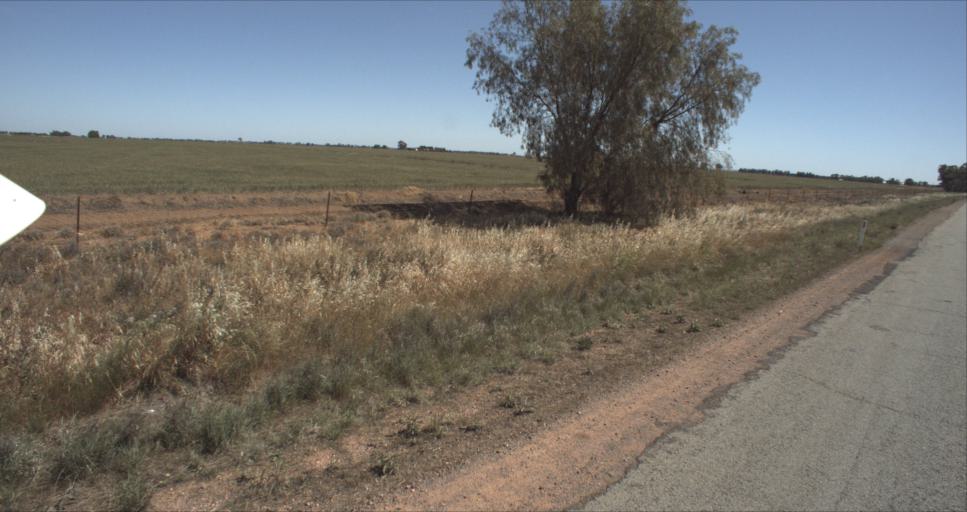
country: AU
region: New South Wales
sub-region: Leeton
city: Leeton
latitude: -34.5594
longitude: 146.3130
